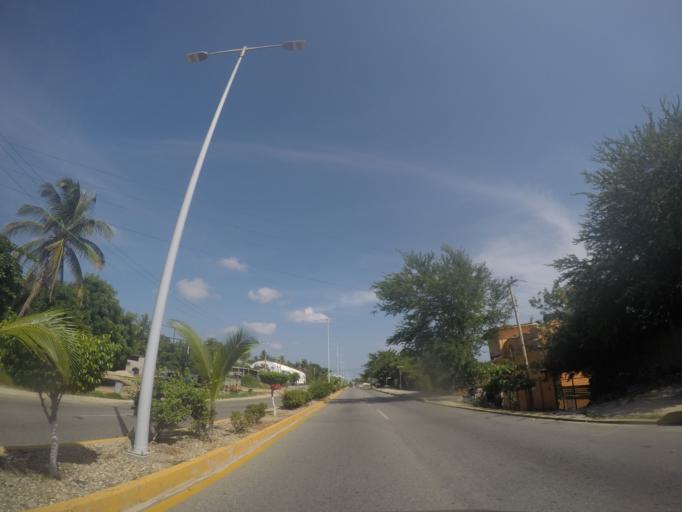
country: MX
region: Oaxaca
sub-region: Santa Maria Colotepec
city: Brisas de Zicatela
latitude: 15.8560
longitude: -97.0556
